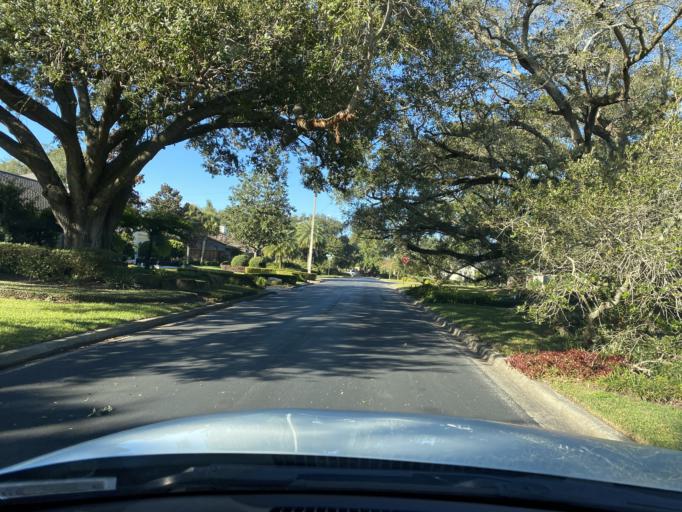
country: US
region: Florida
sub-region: Orange County
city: Orlando
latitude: 28.5547
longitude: -81.4038
